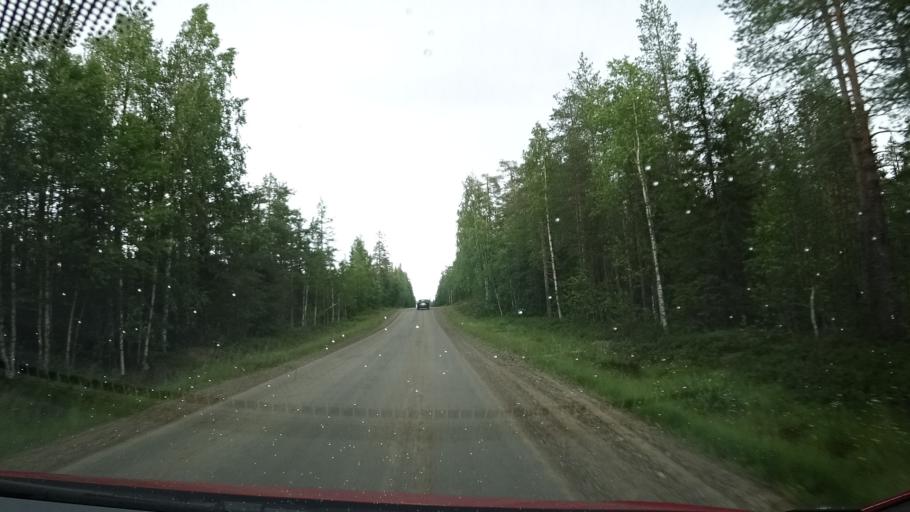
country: FI
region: Kainuu
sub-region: Kehys-Kainuu
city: Kuhmo
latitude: 63.9394
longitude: 29.2098
